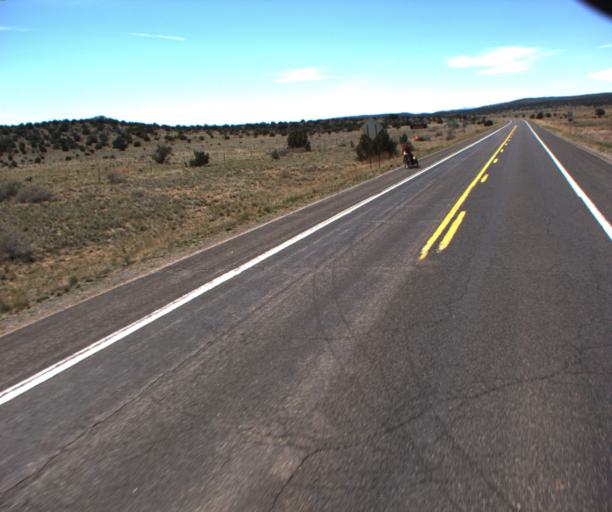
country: US
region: Arizona
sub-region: Mohave County
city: Peach Springs
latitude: 35.5520
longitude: -113.3122
